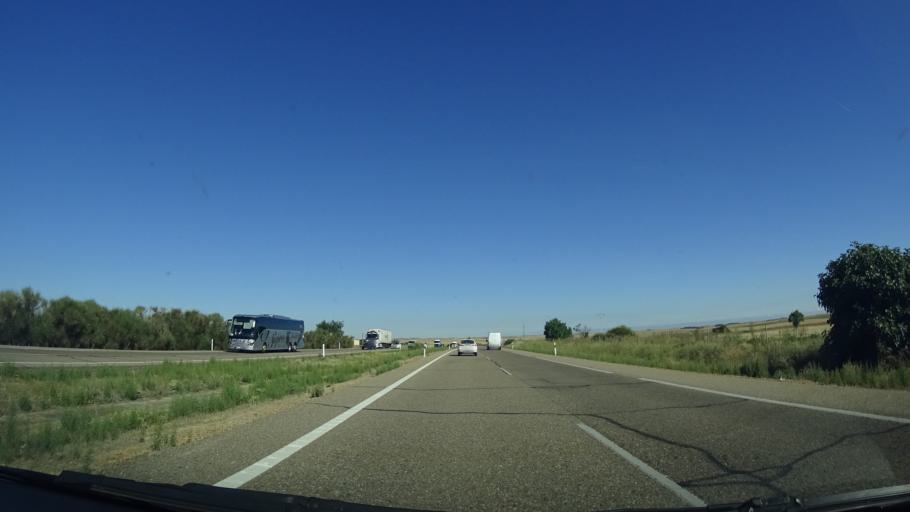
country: ES
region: Castille and Leon
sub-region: Provincia de Zamora
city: Cerecinos de Campos
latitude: 41.8908
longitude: -5.4678
